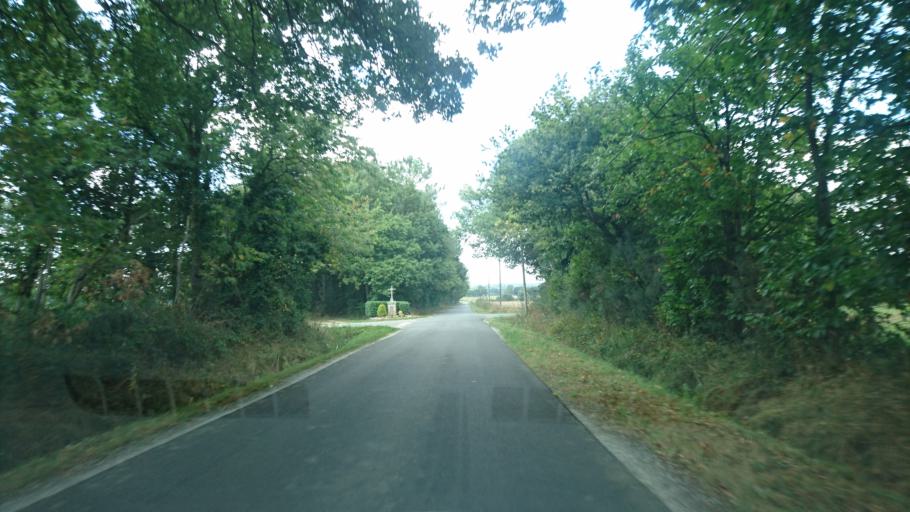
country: FR
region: Brittany
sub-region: Departement d'Ille-et-Vilaine
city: Bains-sur-Oust
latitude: 47.7137
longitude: -2.1045
